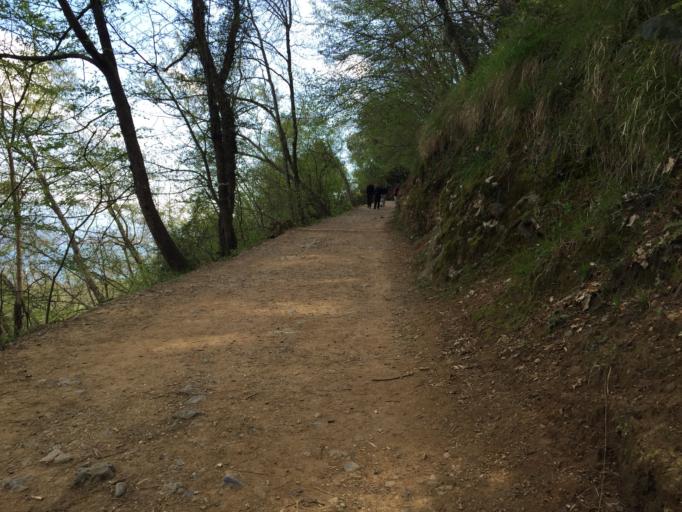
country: IT
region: Liguria
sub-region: Provincia di Genova
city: Camogli
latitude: 44.3276
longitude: 9.1732
